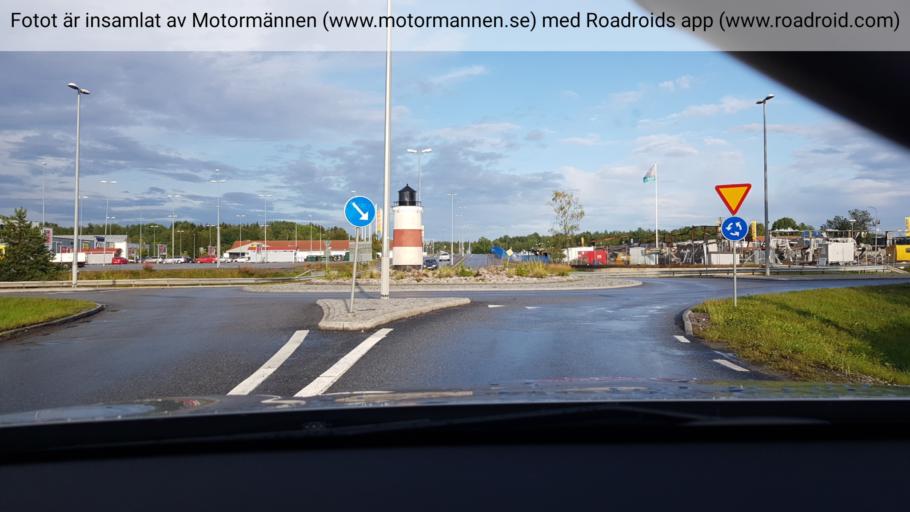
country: SE
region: Stockholm
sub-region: Norrtalje Kommun
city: Norrtalje
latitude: 59.7663
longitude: 18.6906
